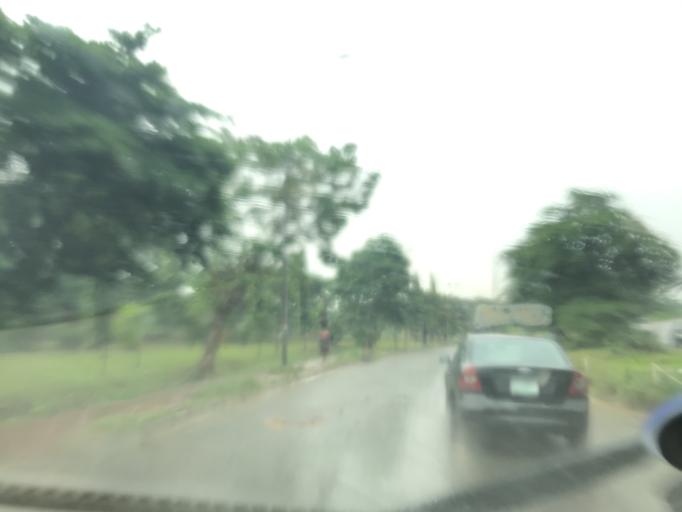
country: NG
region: Lagos
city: Oshodi
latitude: 6.5490
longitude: 3.3373
